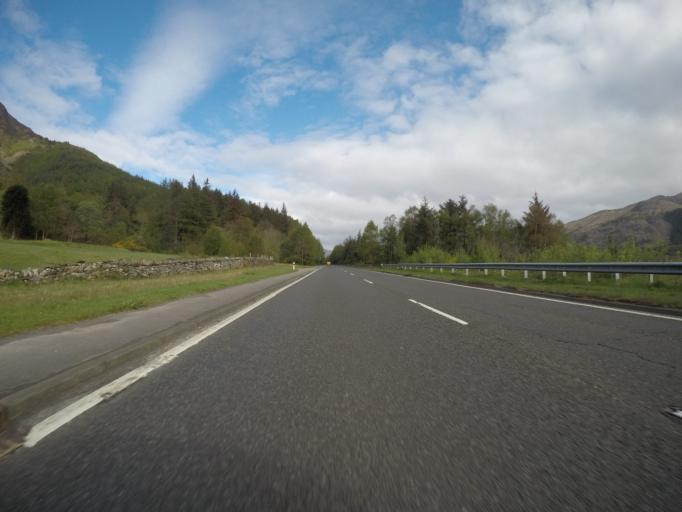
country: GB
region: Scotland
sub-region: Highland
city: Fort William
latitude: 56.6787
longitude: -5.1563
